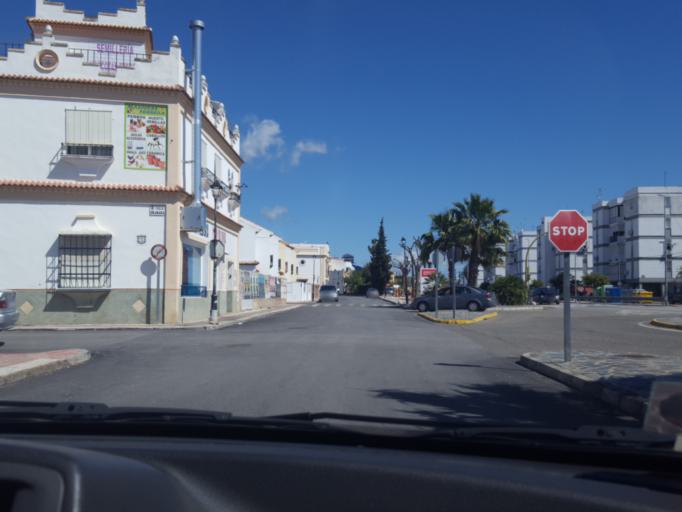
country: ES
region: Andalusia
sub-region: Provincia de Sevilla
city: Acala del Rio
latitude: 37.5192
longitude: -5.9849
